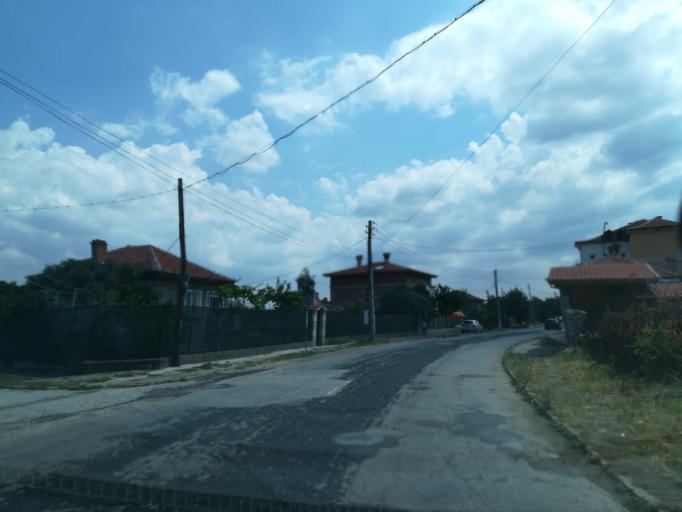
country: BG
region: Plovdiv
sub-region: Obshtina Asenovgrad
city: Asenovgrad
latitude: 41.9316
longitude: 24.9845
